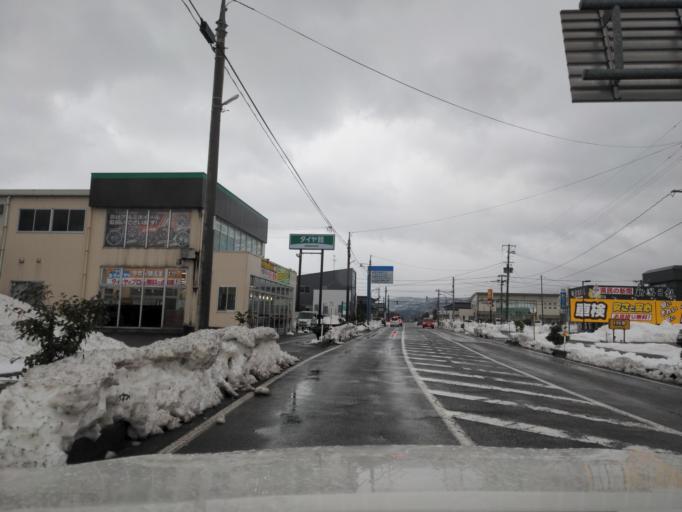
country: JP
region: Niigata
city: Kashiwazaki
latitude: 37.3602
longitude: 138.5639
